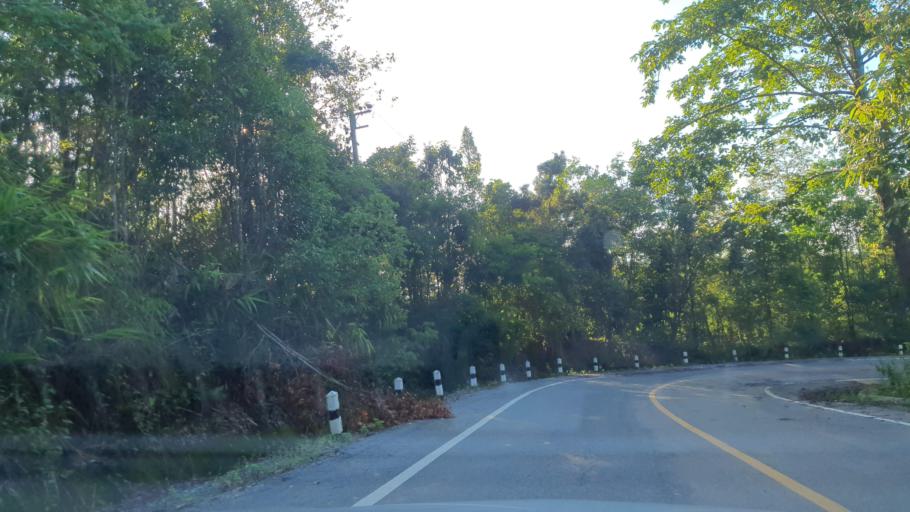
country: TH
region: Chiang Mai
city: Mae On
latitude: 18.8092
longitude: 99.3016
